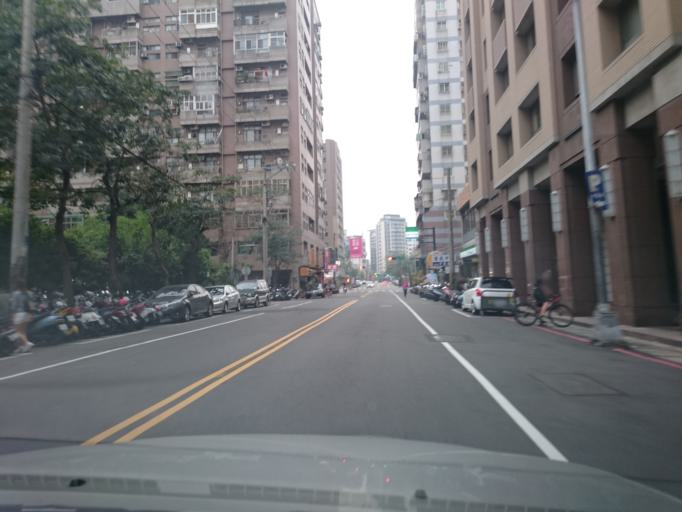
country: TW
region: Taiwan
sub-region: Taichung City
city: Taichung
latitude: 24.1711
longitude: 120.6402
